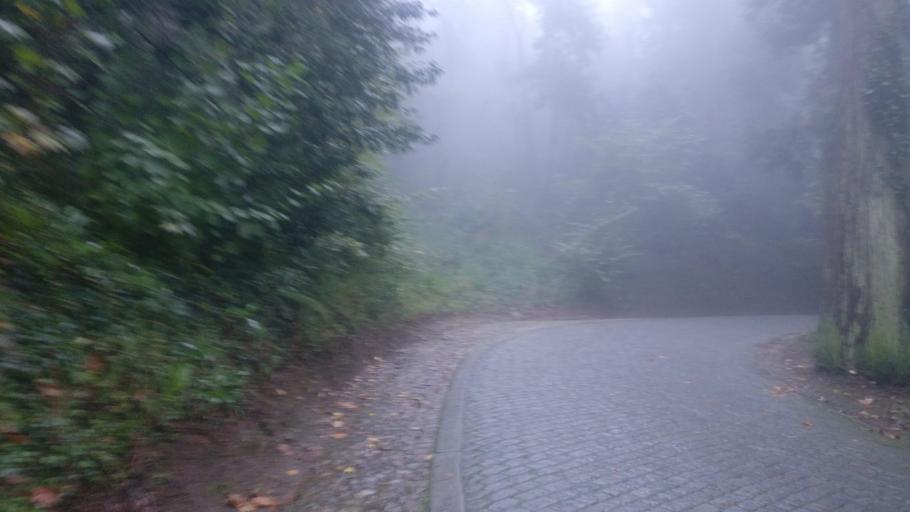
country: PT
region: Aveiro
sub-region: Mealhada
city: Pampilhosa do Botao
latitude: 40.3774
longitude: -8.3634
